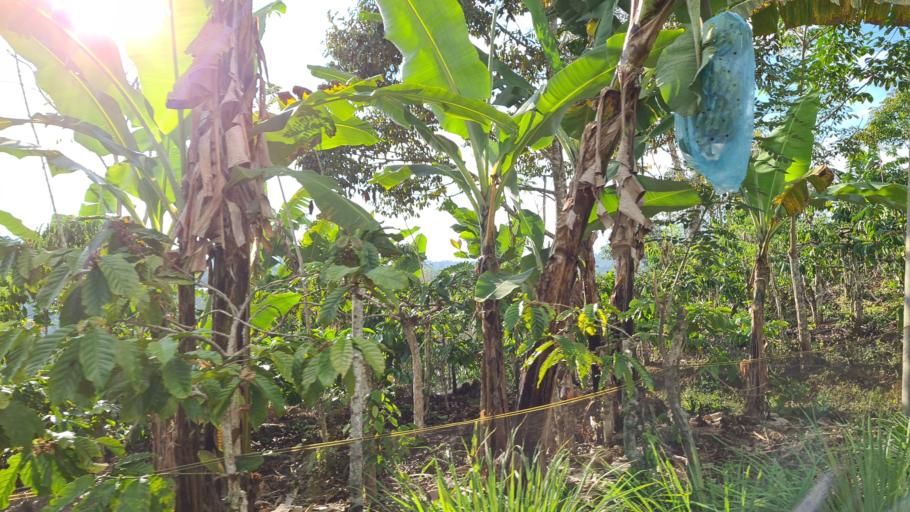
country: ID
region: Lampung
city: Kenali
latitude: -5.0962
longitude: 104.3973
